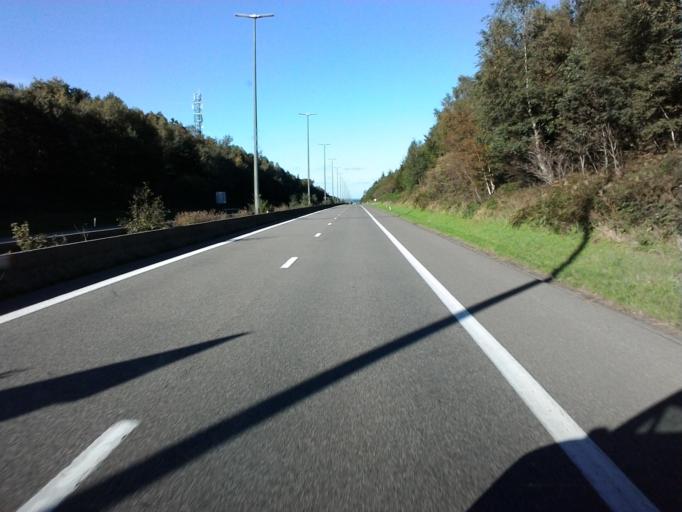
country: BE
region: Wallonia
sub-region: Province du Luxembourg
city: Bastogne
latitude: 50.0550
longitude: 5.7207
